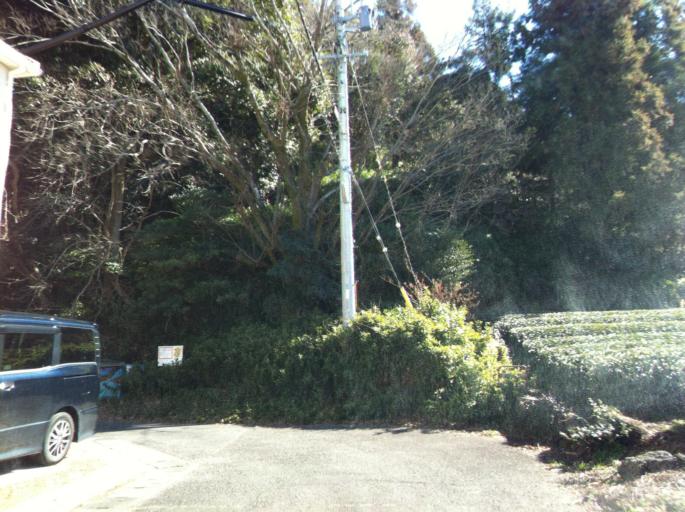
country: JP
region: Shizuoka
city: Shizuoka-shi
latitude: 35.0373
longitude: 138.4015
